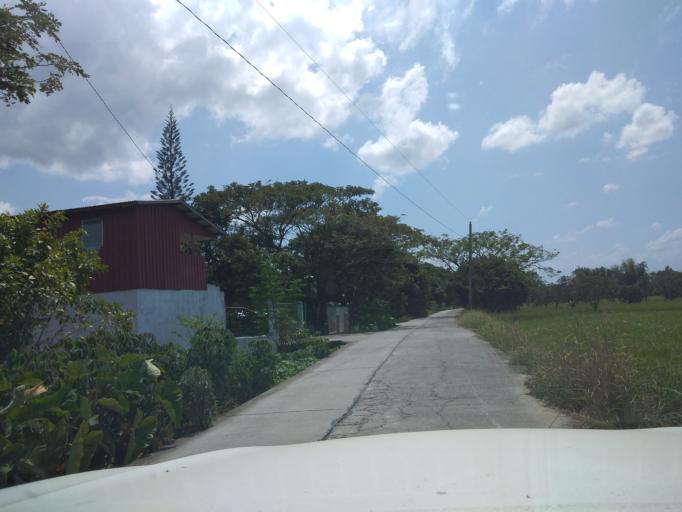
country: PH
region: Central Luzon
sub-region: Province of Pampanga
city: Lourdes
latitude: 15.0119
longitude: 120.8672
